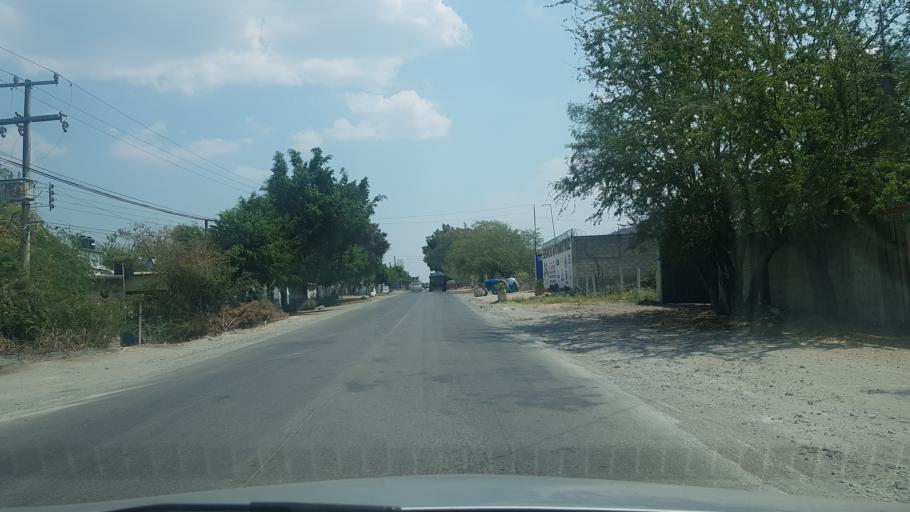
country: MX
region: Morelos
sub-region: Tlaltizapan de Zapata
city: Colonia Palo Prieto (Chipitongo)
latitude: 18.7235
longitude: -99.1221
